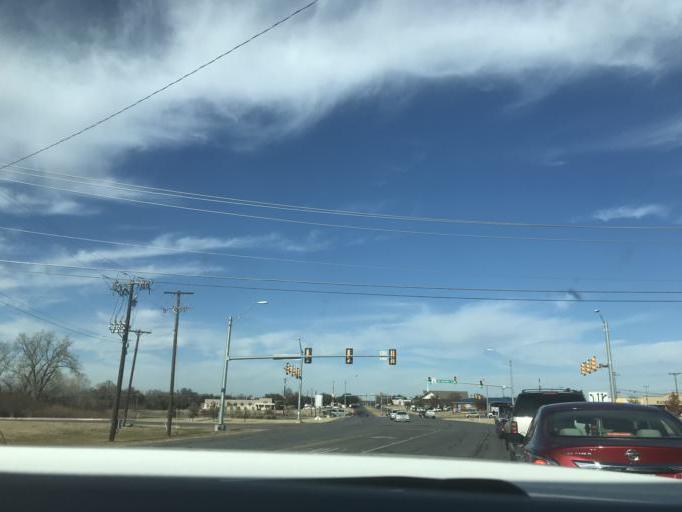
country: US
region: Texas
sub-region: Erath County
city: Stephenville
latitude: 32.2246
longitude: -98.2329
